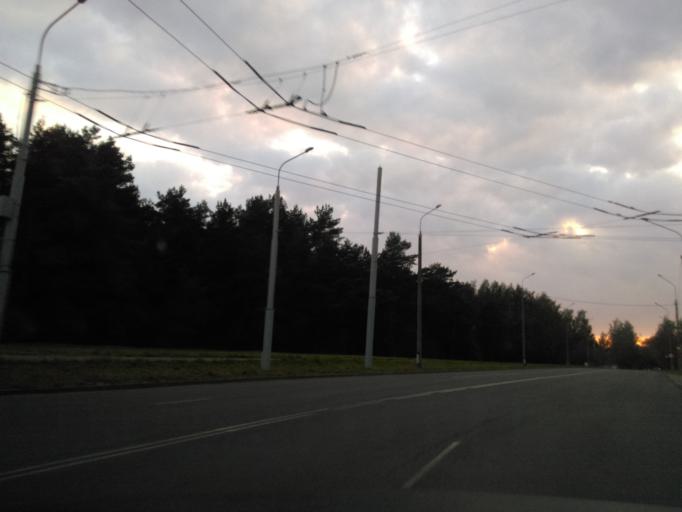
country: BY
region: Minsk
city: Vyaliki Trastsyanets
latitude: 53.8858
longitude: 27.6491
